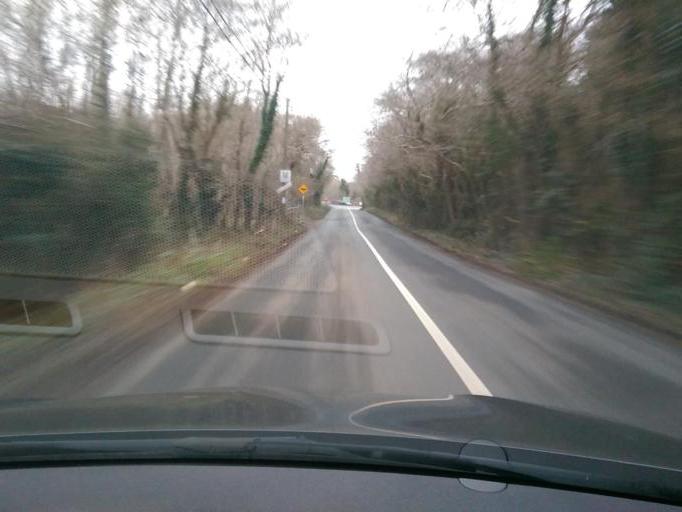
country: IE
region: Connaught
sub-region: County Galway
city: Moycullen
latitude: 53.3121
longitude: -9.1490
